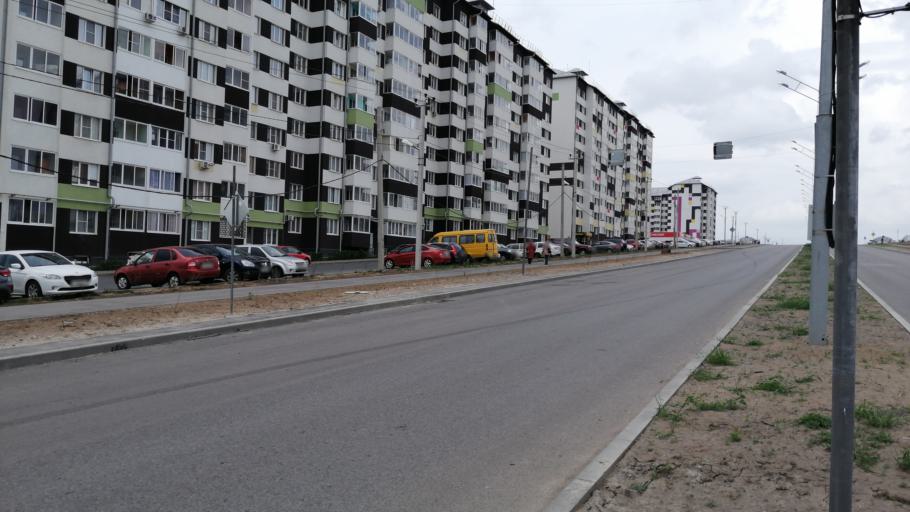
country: RU
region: Kursk
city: Kursk
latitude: 51.7182
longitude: 36.1191
